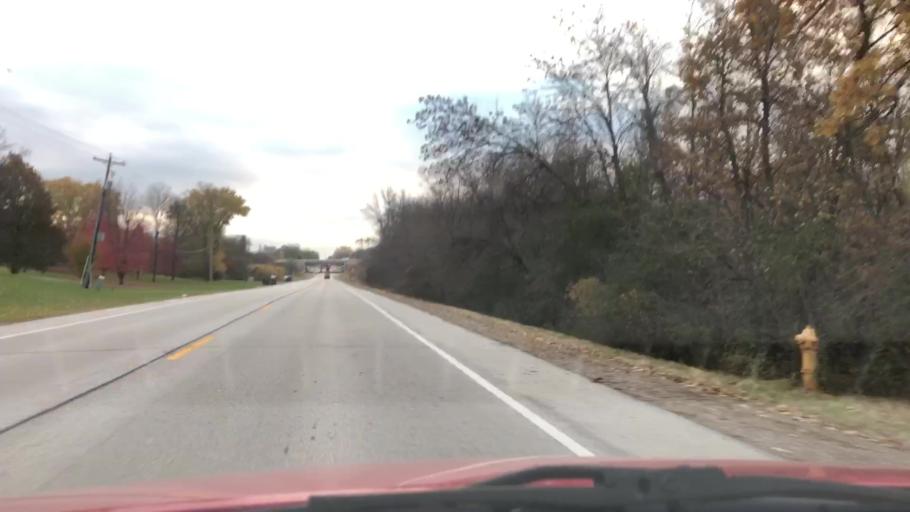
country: US
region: Wisconsin
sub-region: Brown County
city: De Pere
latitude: 44.4452
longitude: -88.1018
